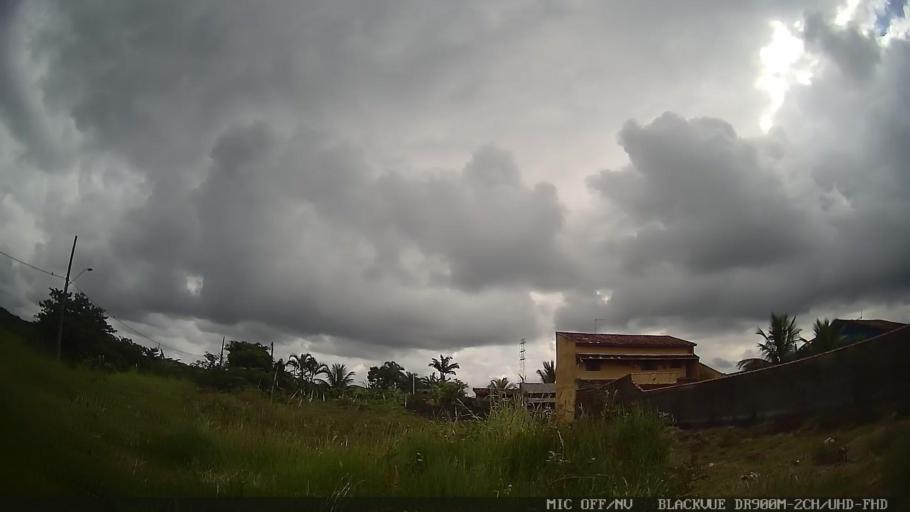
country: BR
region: Sao Paulo
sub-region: Itanhaem
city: Itanhaem
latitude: -24.2033
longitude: -46.8464
